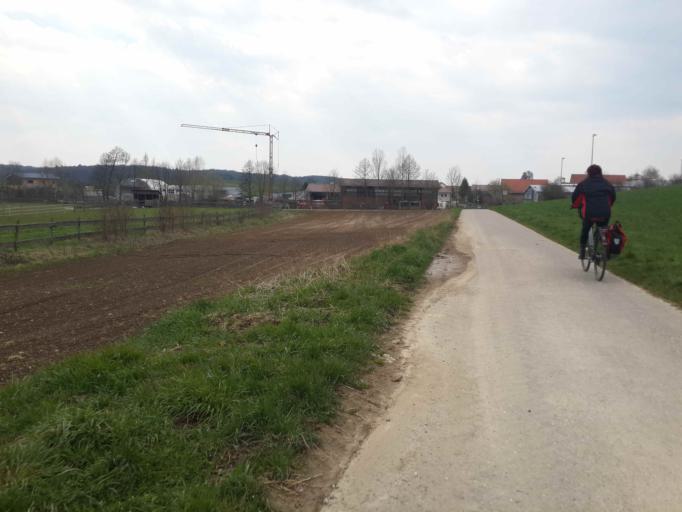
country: DE
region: Baden-Wuerttemberg
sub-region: Regierungsbezirk Stuttgart
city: Eppingen
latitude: 49.1630
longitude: 8.8939
